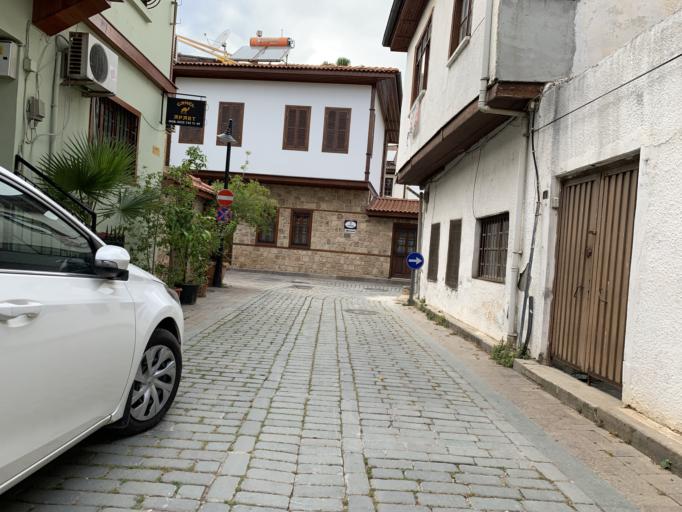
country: TR
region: Antalya
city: Antalya
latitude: 36.8812
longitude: 30.7055
